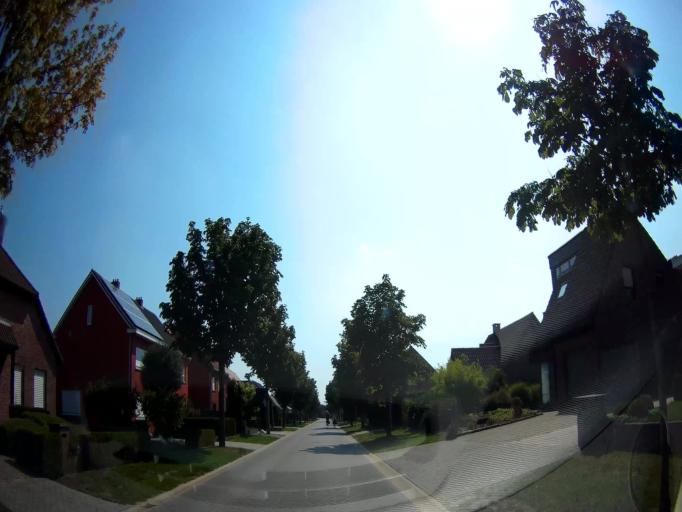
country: BE
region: Flanders
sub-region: Provincie Antwerpen
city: Oud-Turnhout
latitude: 51.3096
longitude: 4.9891
